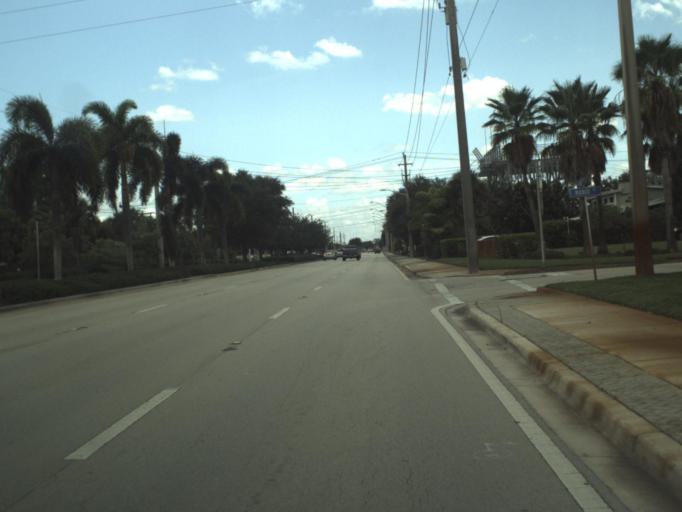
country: US
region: Florida
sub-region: Martin County
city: Stuart
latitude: 27.1850
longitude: -80.2532
